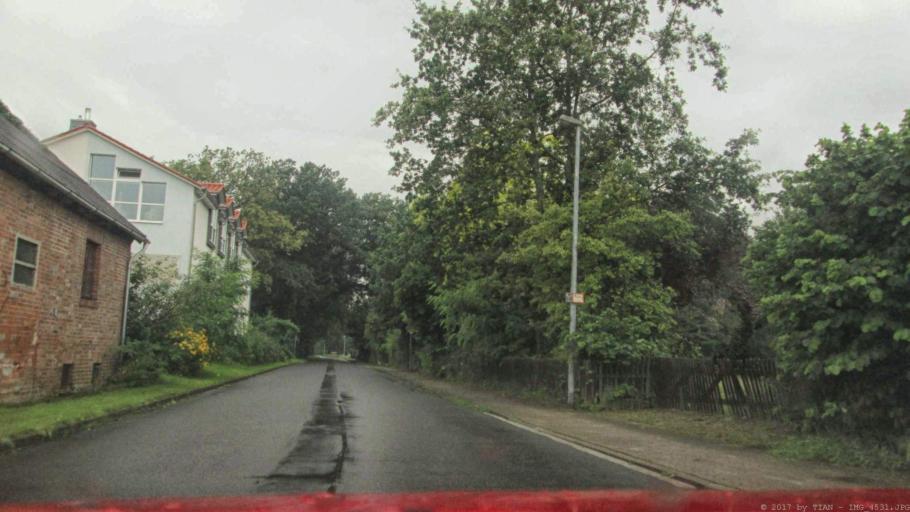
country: DE
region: Lower Saxony
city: Jembke
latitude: 52.4760
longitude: 10.7648
